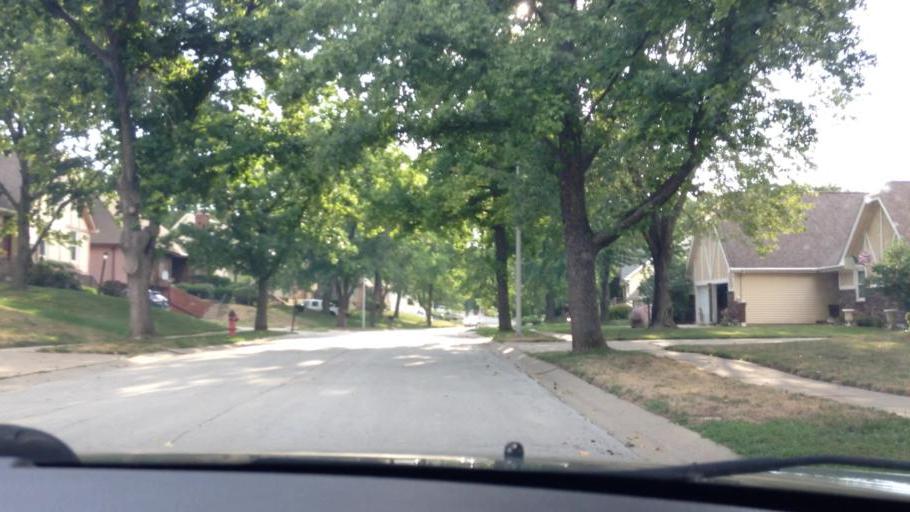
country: US
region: Missouri
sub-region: Platte County
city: Riverside
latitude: 39.2158
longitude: -94.6366
